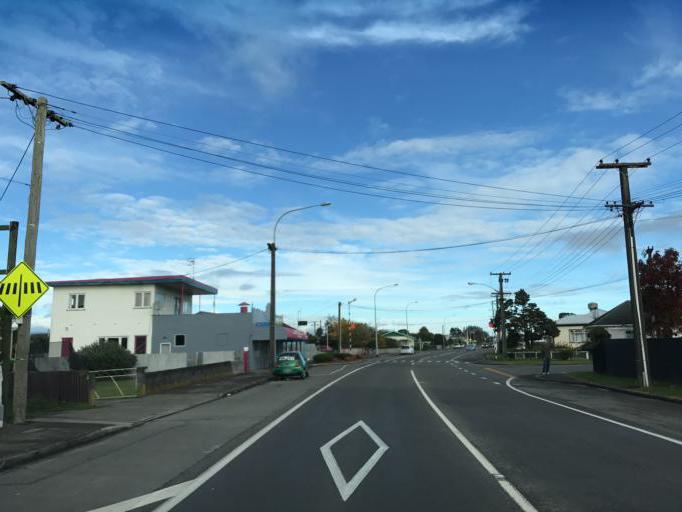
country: NZ
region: Manawatu-Wanganui
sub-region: Horowhenua District
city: Foxton
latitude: -40.4727
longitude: 175.2858
